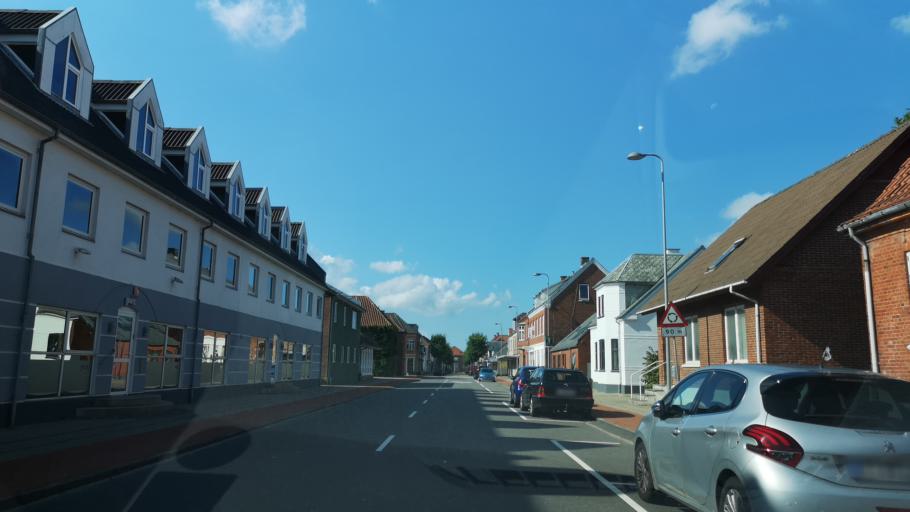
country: DK
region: Central Jutland
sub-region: Ringkobing-Skjern Kommune
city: Skjern
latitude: 55.9495
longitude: 8.4969
